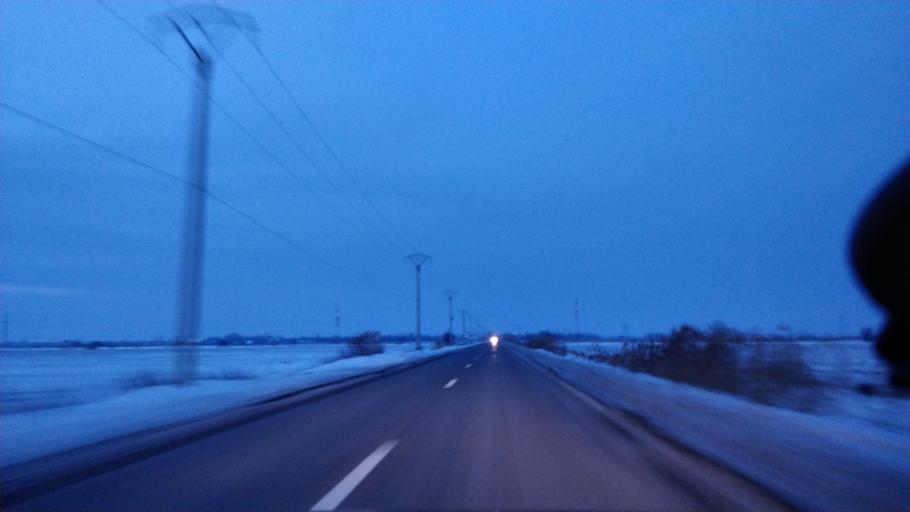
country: RO
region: Vrancea
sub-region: Comuna Nanesti
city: Nanesti
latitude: 45.5788
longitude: 27.4974
